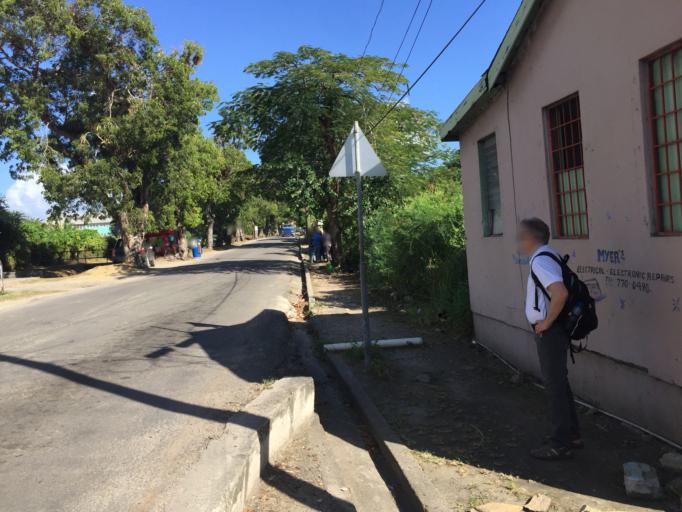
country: AG
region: Saint John
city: Saint John's
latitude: 17.1259
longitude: -61.8447
